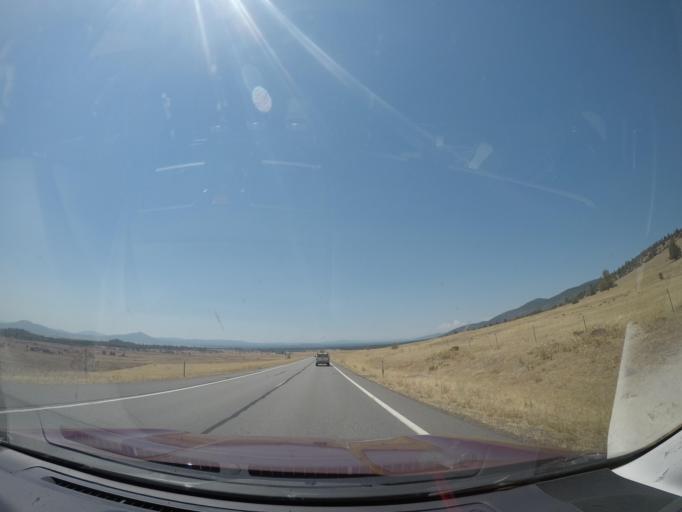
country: US
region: California
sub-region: Shasta County
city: Burney
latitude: 41.0956
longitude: -121.2814
